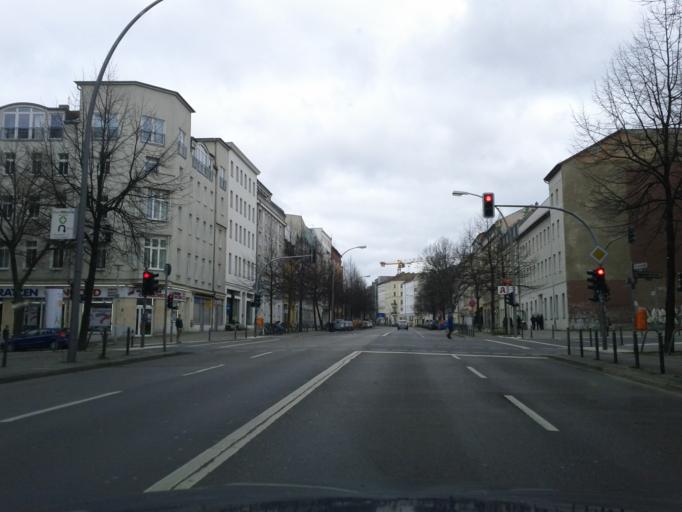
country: DE
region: Berlin
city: Berlin
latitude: 52.5347
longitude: 13.3982
